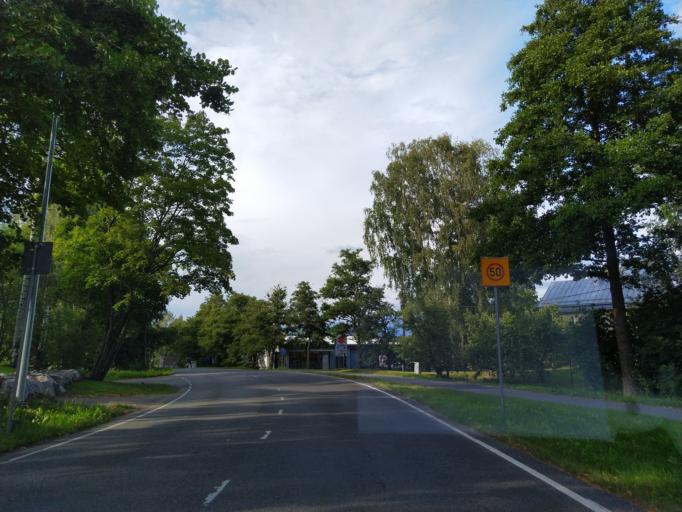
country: FI
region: Varsinais-Suomi
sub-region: Turku
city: Turku
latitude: 60.4252
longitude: 22.2270
